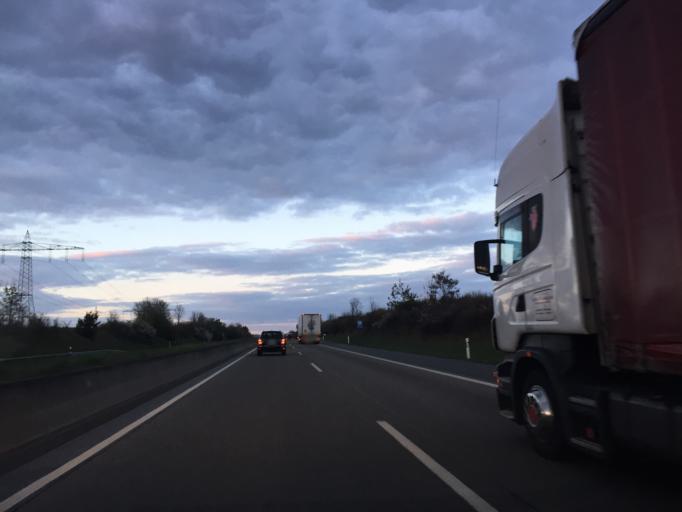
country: DE
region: Thuringia
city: Gerstungen
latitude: 50.9669
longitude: 10.0609
